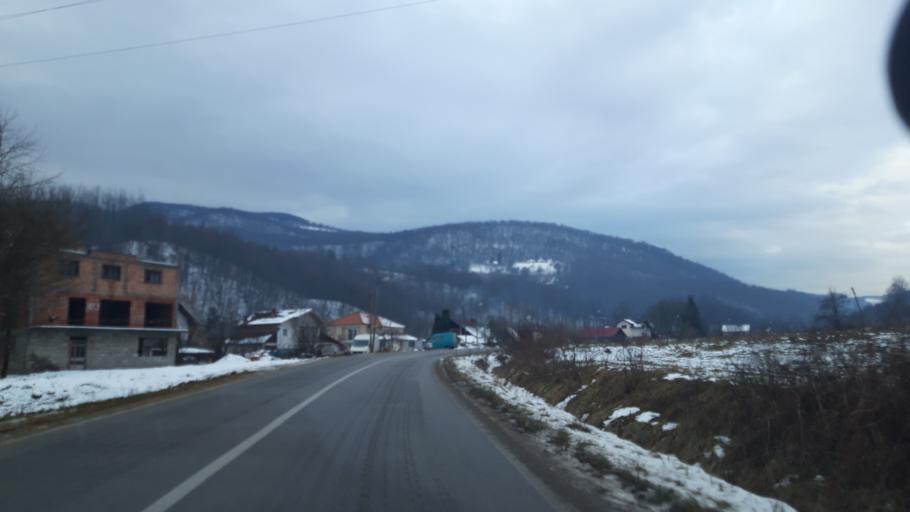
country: BA
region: Republika Srpska
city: Milici
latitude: 44.1641
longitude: 19.0490
